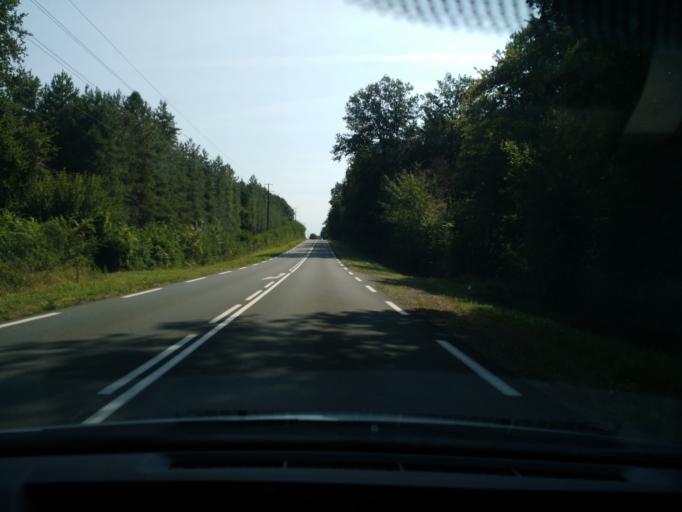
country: FR
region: Pays de la Loire
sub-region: Departement de Maine-et-Loire
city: Bauge-en-Anjou
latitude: 47.5329
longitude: -0.0622
